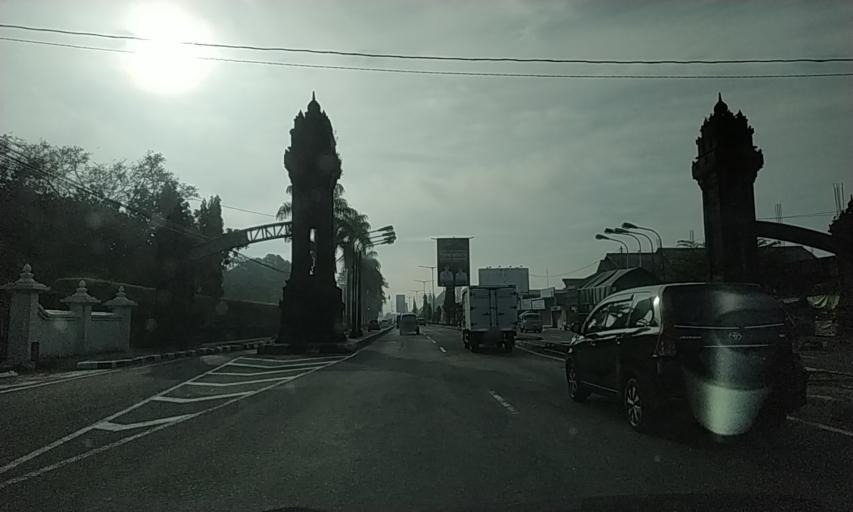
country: ID
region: Central Java
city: Candi Prambanan
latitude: -7.7552
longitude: 110.4915
